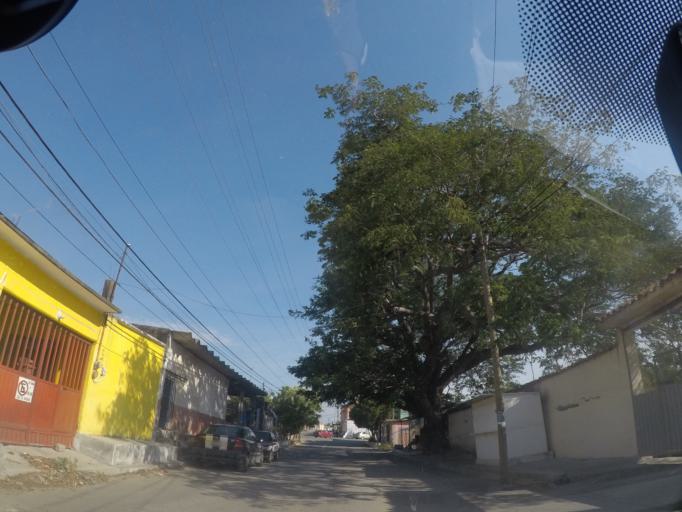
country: MX
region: Oaxaca
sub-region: Salina Cruz
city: Salina Cruz
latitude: 16.1966
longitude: -95.2025
